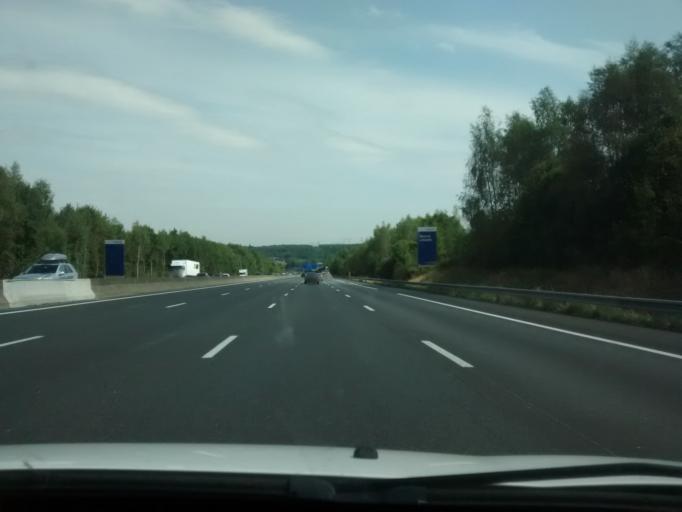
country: FR
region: Ile-de-France
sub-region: Departement de l'Essonne
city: Les Ulis
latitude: 48.6489
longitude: 2.1683
